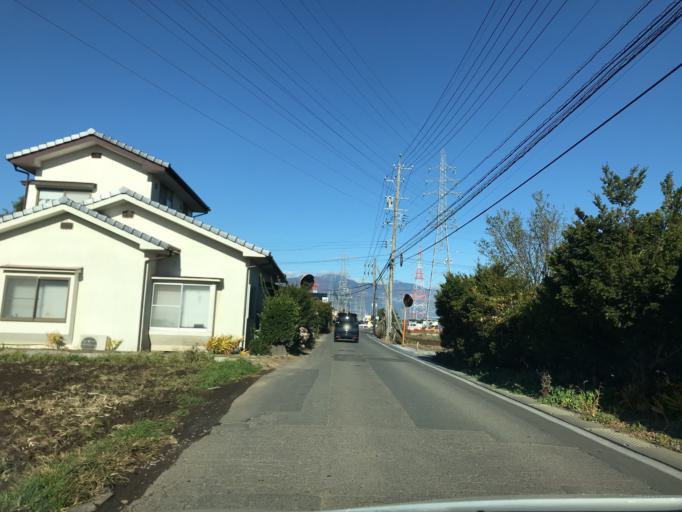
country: JP
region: Nagano
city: Shiojiri
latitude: 36.1225
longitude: 137.9402
